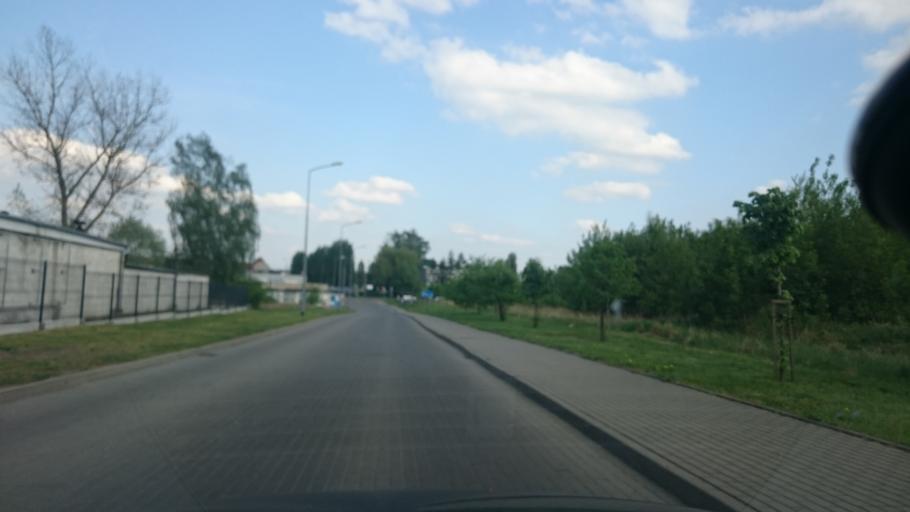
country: PL
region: Kujawsko-Pomorskie
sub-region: Grudziadz
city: Grudziadz
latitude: 53.4717
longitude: 18.7496
